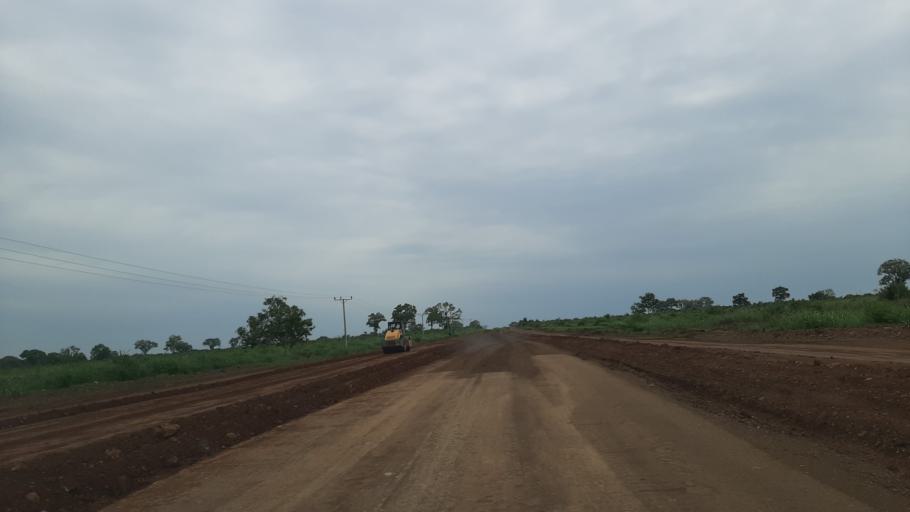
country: ET
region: Gambela
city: Gambela
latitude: 8.1829
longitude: 34.4956
